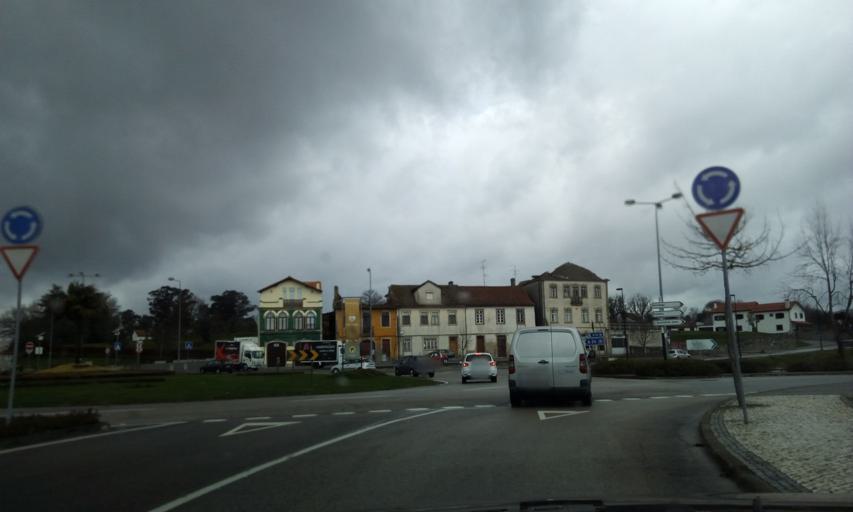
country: PT
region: Viseu
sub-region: Viseu
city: Viseu
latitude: 40.6647
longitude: -7.9073
